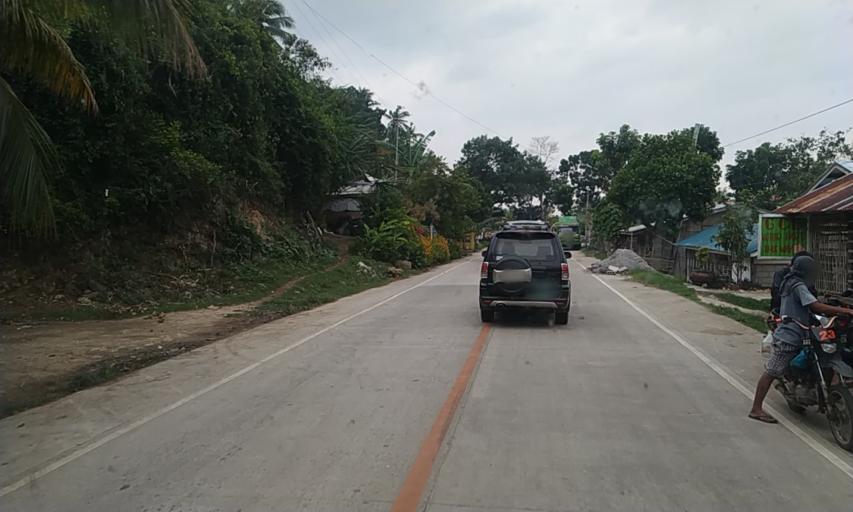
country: PH
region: Central Visayas
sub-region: Province of Negros Oriental
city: Basak
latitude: 10.2104
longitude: 123.3020
